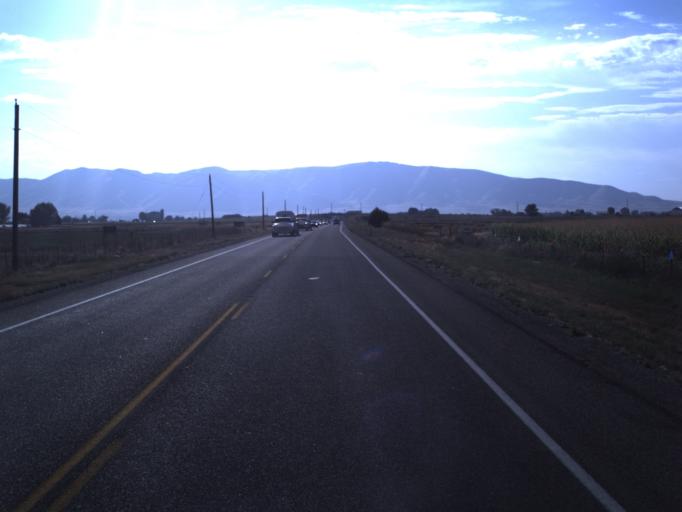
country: US
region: Utah
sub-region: Utah County
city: Salem
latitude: 40.0853
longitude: -111.6898
